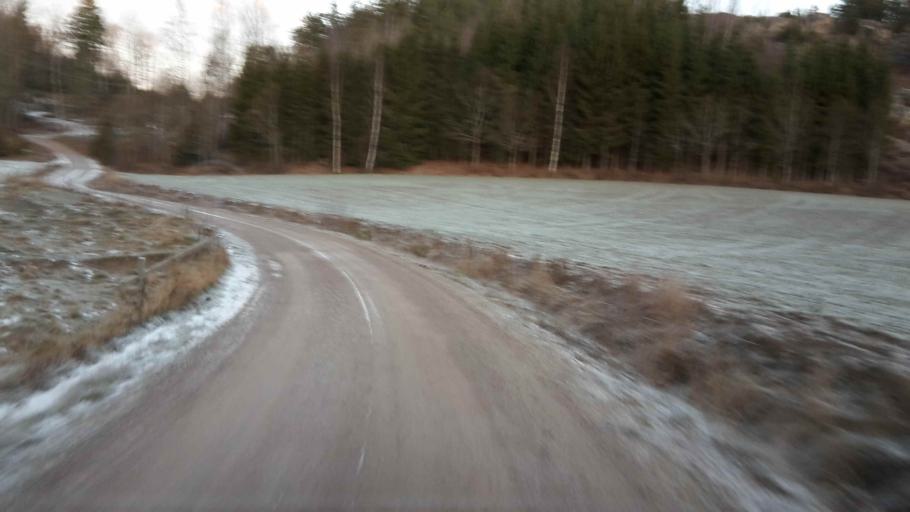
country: SE
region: OEstergoetland
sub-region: Atvidabergs Kommun
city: Atvidaberg
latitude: 58.2695
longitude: 16.1306
